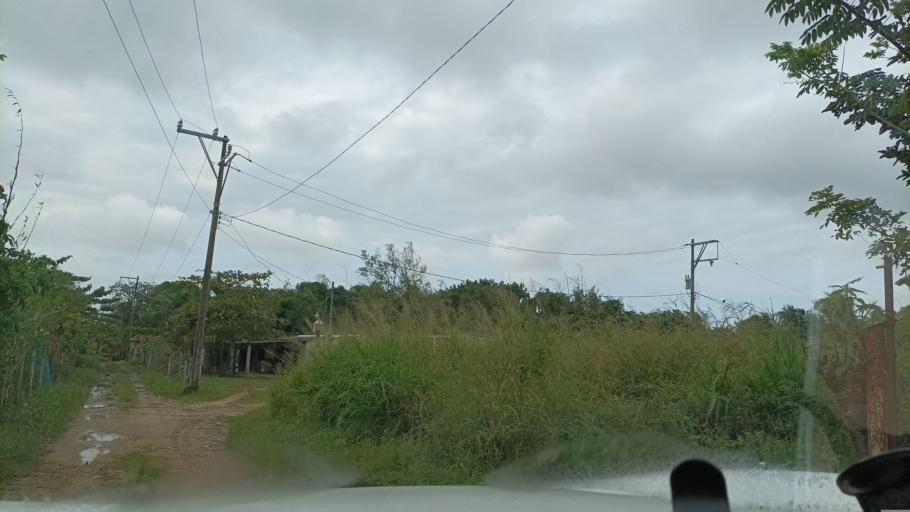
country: MX
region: Veracruz
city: Villa Nanchital
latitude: 18.0565
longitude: -94.4114
